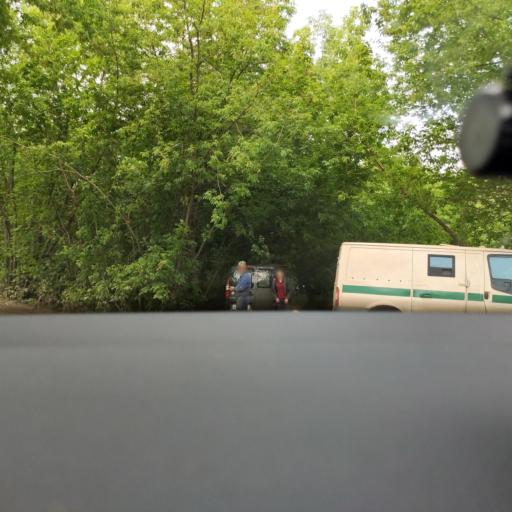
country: RU
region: Moskovskaya
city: Fili
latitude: 55.7469
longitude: 37.4532
